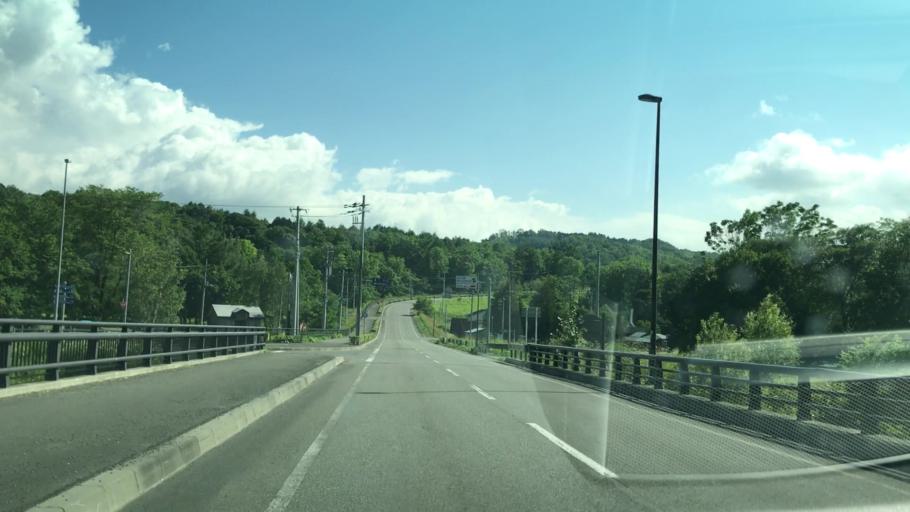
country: JP
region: Hokkaido
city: Shimo-furano
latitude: 42.8714
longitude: 142.4427
